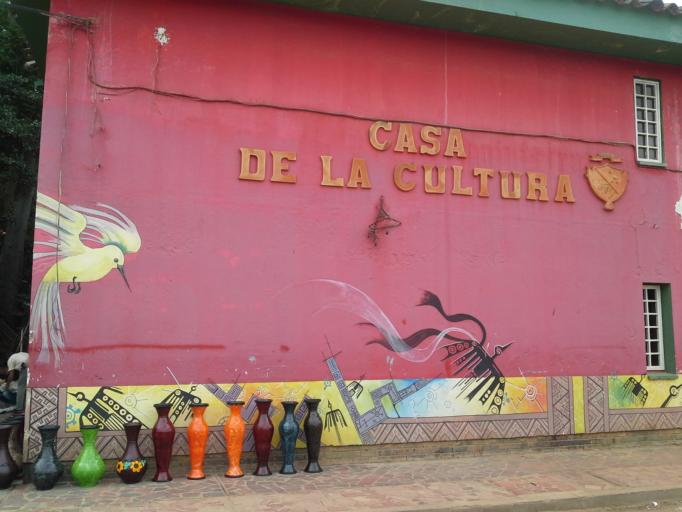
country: CO
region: Boyaca
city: Raquira
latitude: 5.5400
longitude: -73.6329
